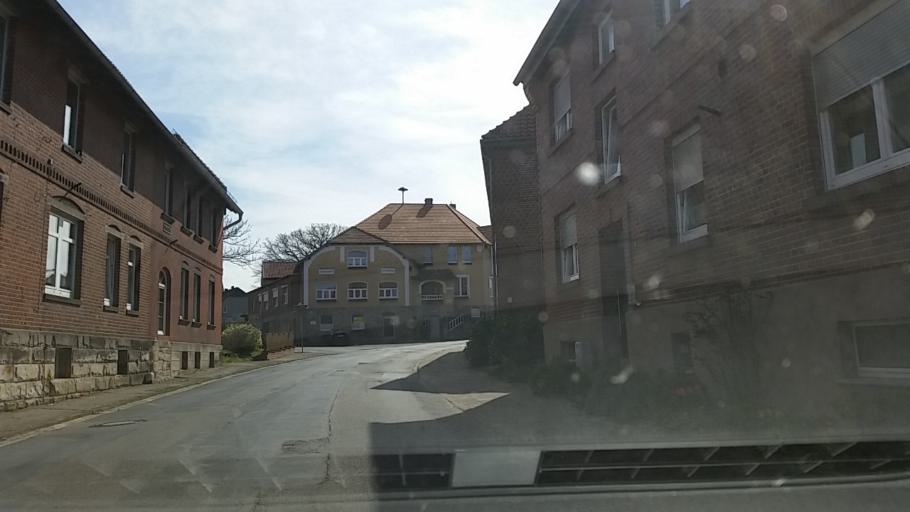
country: DE
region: Lower Saxony
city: Querenhorst
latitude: 52.3590
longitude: 10.9682
